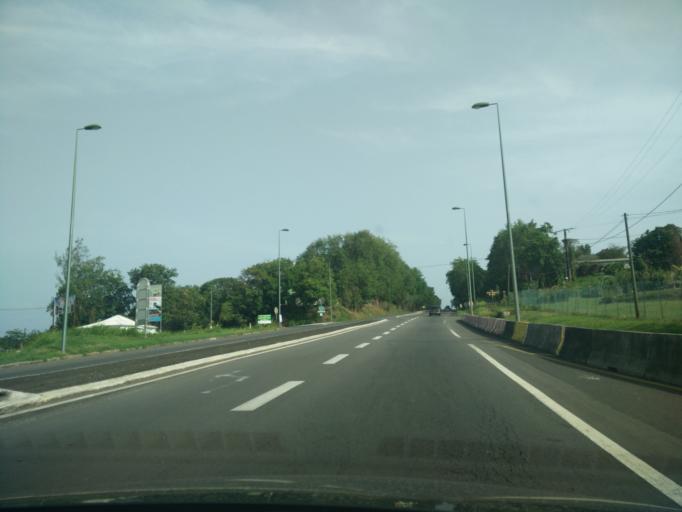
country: GP
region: Guadeloupe
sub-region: Guadeloupe
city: Petit-Bourg
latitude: 16.1469
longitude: -61.5833
